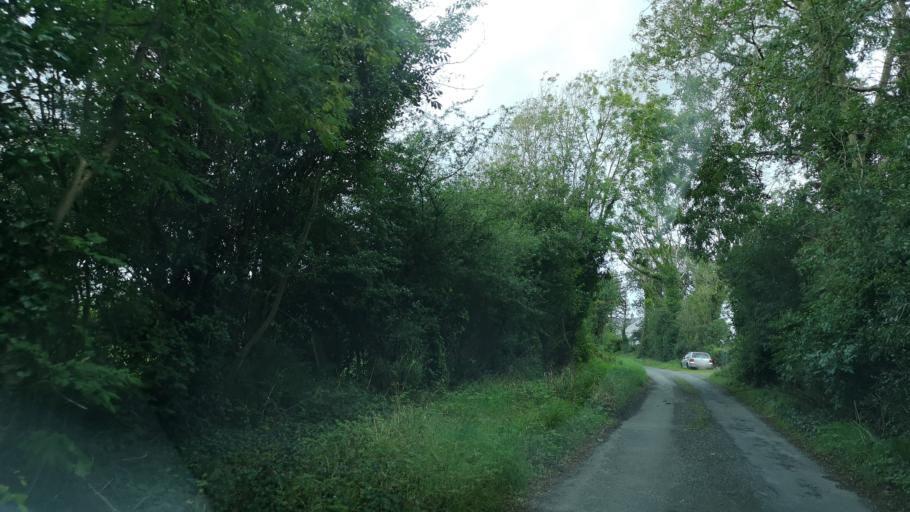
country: IE
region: Connaught
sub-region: County Galway
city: Athenry
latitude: 53.2991
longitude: -8.6946
